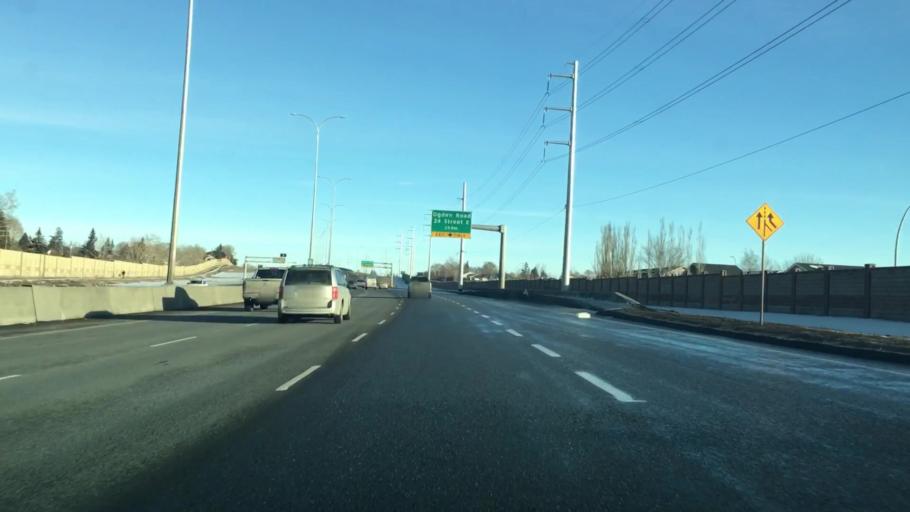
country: CA
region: Alberta
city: Calgary
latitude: 50.9793
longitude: -114.0096
